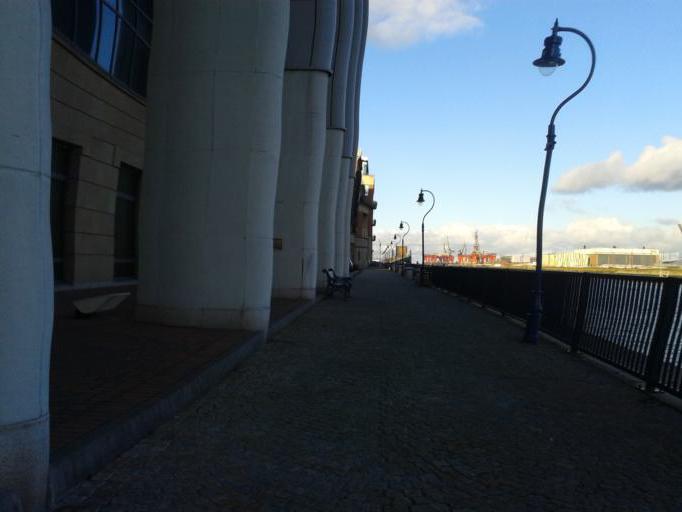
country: GB
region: Northern Ireland
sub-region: City of Belfast
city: Belfast
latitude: 54.6061
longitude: -5.9181
